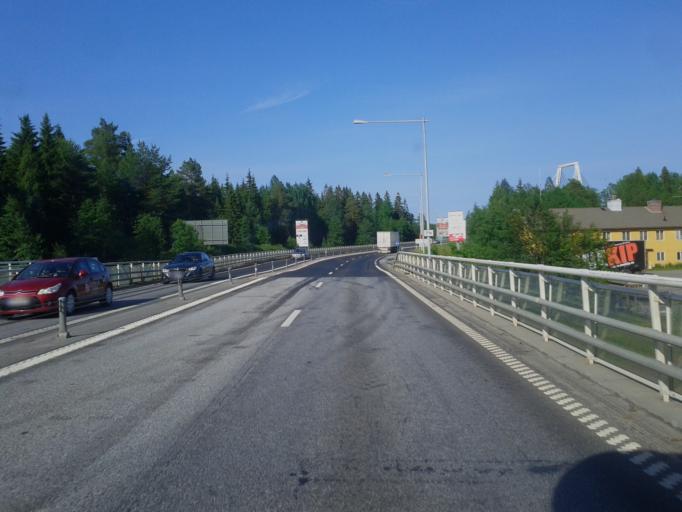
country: SE
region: Vaesterbotten
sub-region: Umea Kommun
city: Umea
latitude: 63.8000
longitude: 20.2872
